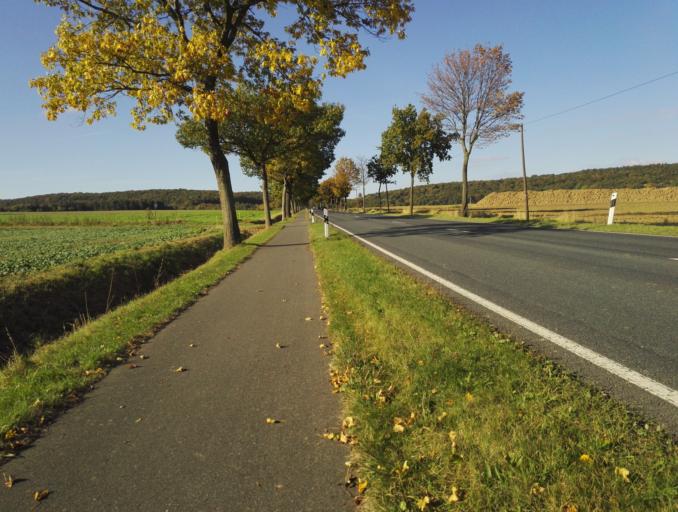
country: DE
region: Lower Saxony
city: Holle
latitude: 52.1146
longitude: 10.1041
